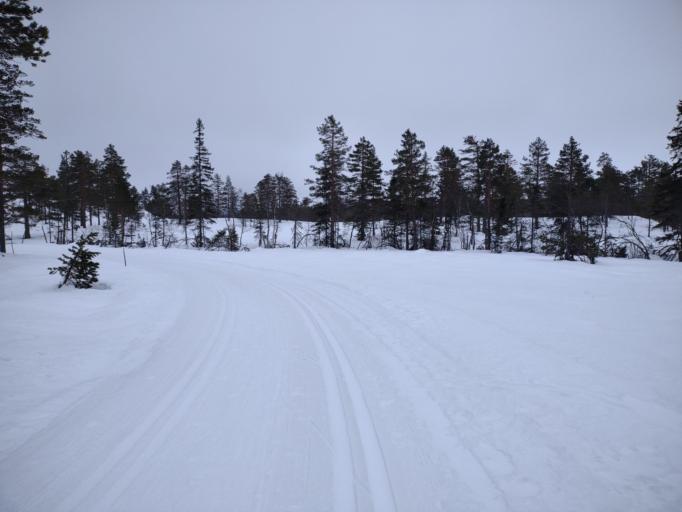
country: NO
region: Buskerud
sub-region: Flesberg
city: Lampeland
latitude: 59.7940
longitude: 9.4393
